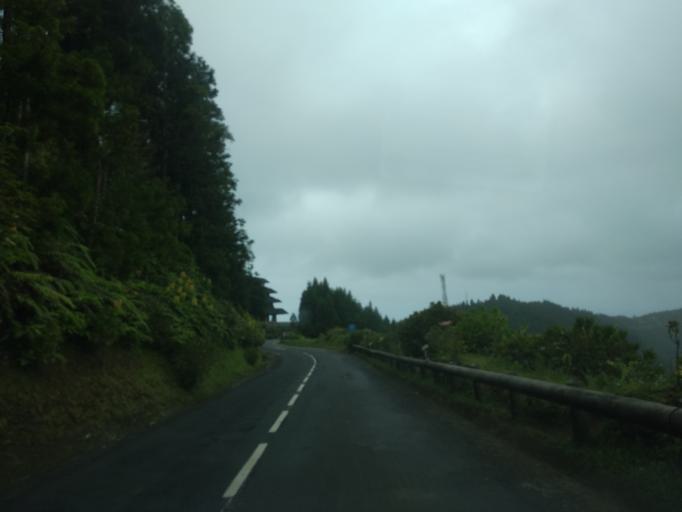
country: PT
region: Azores
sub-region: Ponta Delgada
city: Arrifes
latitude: 37.8392
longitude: -25.7925
